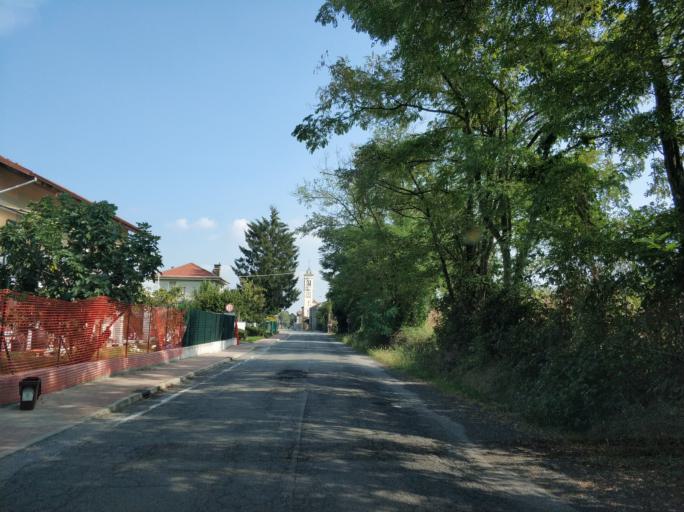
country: IT
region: Piedmont
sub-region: Provincia di Torino
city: San Maurizio
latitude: 45.2371
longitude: 7.6327
